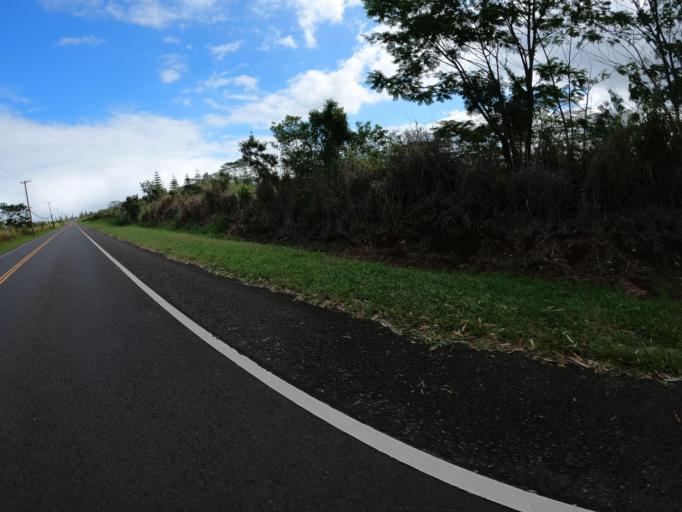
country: US
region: Hawaii
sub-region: Honolulu County
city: Whitmore Village
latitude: 21.5122
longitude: -158.0157
